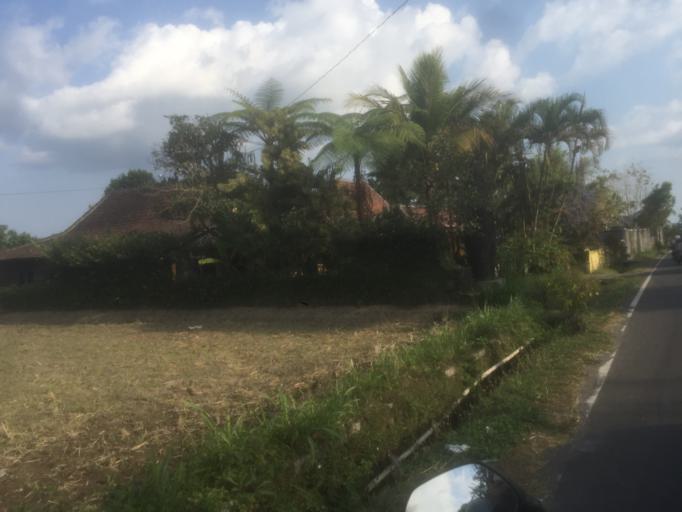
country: ID
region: Daerah Istimewa Yogyakarta
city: Sleman
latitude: -7.6520
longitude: 110.4234
